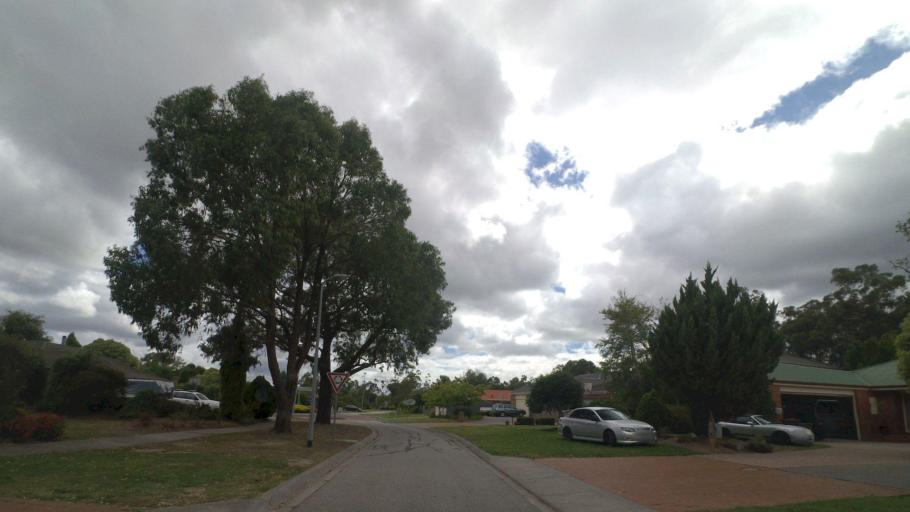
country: AU
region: Victoria
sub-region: Knox
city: The Basin
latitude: -37.8396
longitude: 145.3086
